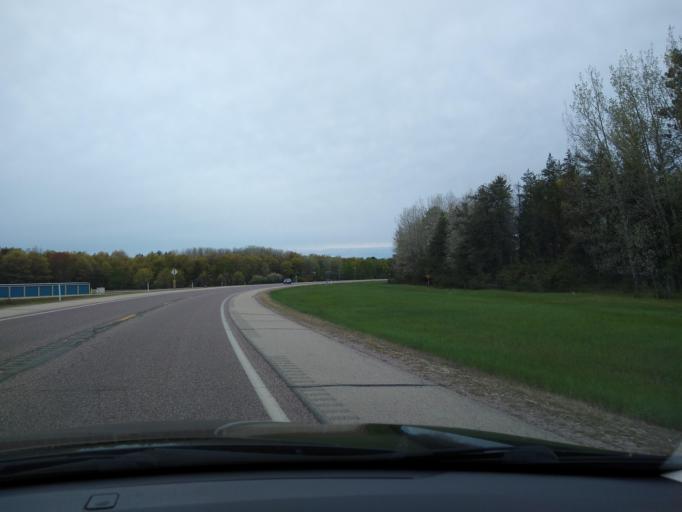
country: US
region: Michigan
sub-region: Delta County
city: Gladstone
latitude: 45.8564
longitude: -87.0602
